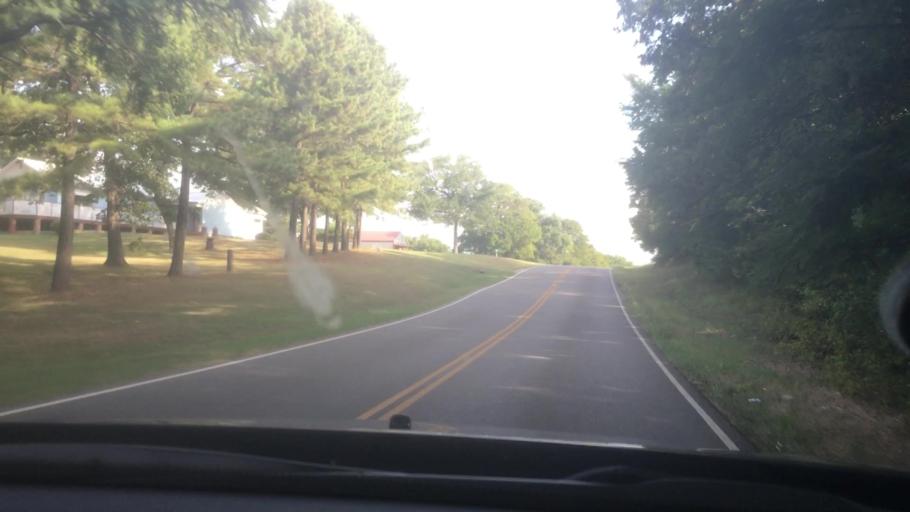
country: US
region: Oklahoma
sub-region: Pontotoc County
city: Ada
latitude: 34.7354
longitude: -96.6711
